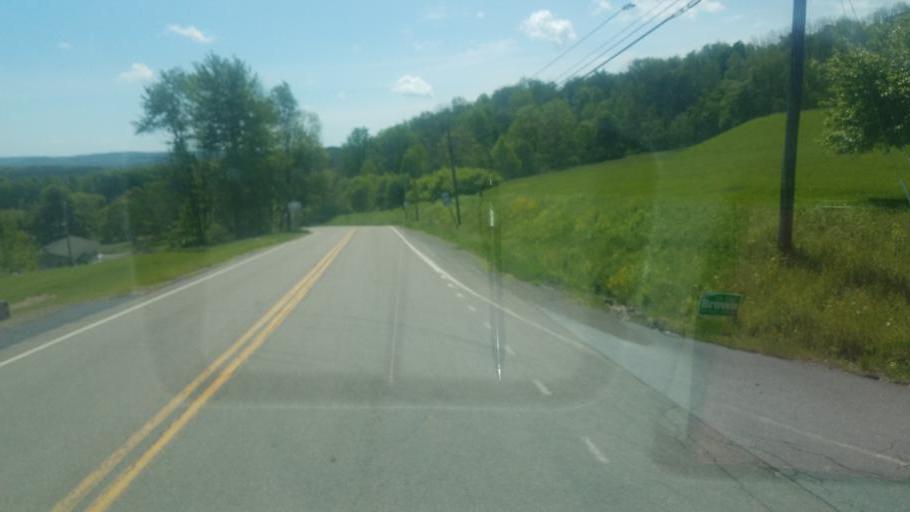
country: US
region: Pennsylvania
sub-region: Tioga County
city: Wellsboro
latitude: 41.7341
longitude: -77.3534
